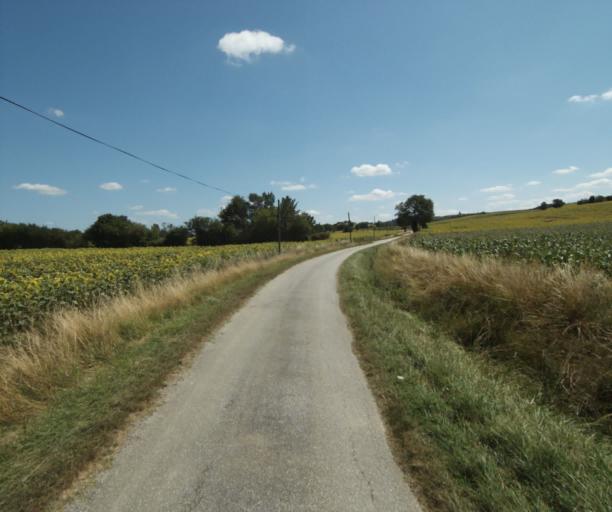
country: FR
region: Midi-Pyrenees
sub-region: Departement de la Haute-Garonne
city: Saint-Felix-Lauragais
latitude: 43.4710
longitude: 1.8854
